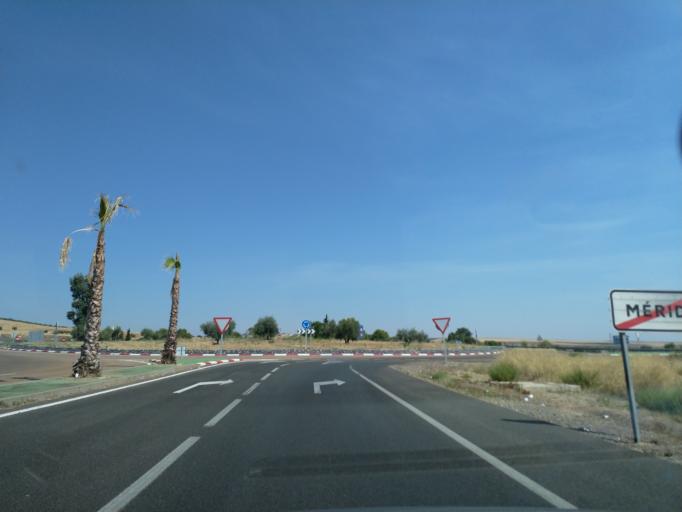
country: ES
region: Extremadura
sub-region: Provincia de Badajoz
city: Merida
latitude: 38.9394
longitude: -6.3436
